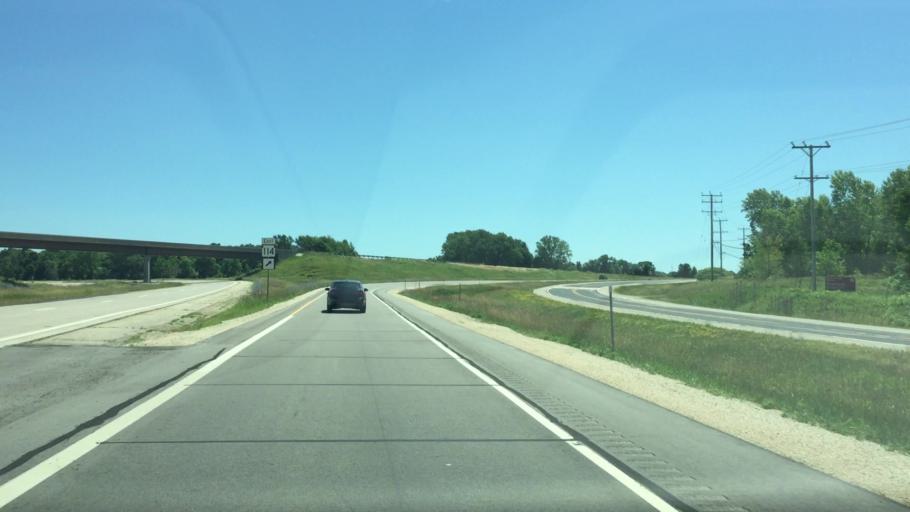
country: US
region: Wisconsin
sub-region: Outagamie County
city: Combined Locks
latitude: 44.2072
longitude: -88.3363
